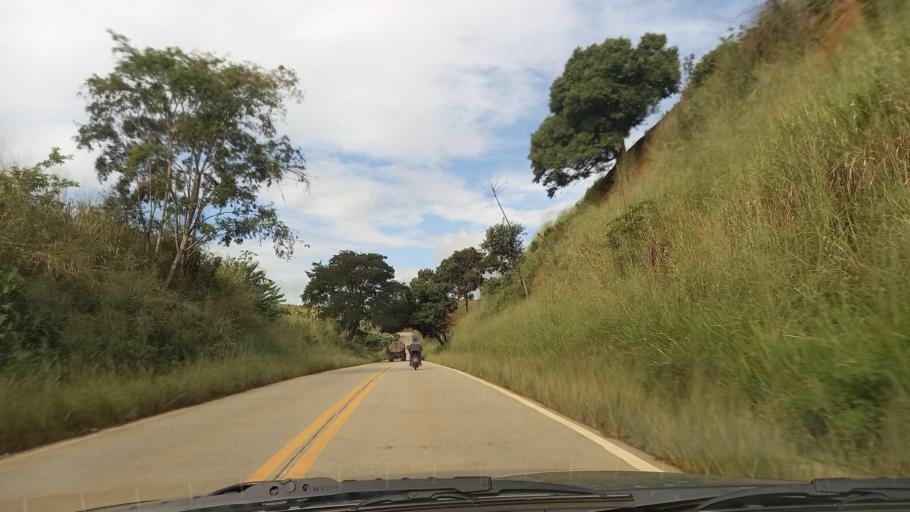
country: BR
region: Pernambuco
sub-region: Maraial
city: Maraial
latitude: -8.7493
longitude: -35.8127
